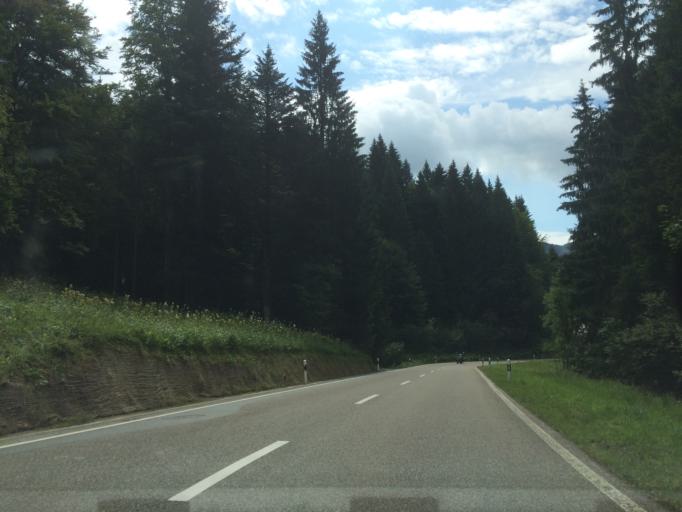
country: CH
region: Appenzell Ausserrhoden
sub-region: Bezirk Hinterland
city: Urnasch
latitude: 47.2594
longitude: 9.3100
